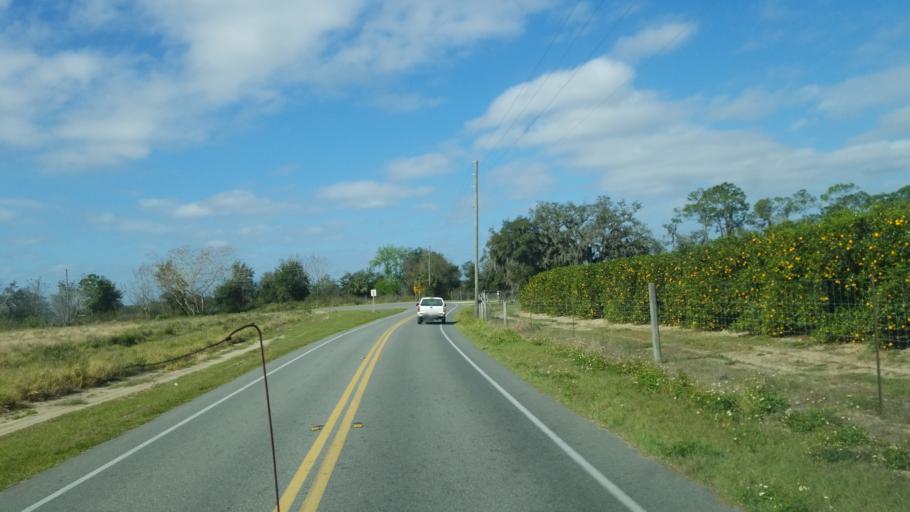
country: US
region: Florida
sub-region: Polk County
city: Babson Park
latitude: 27.9252
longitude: -81.4829
